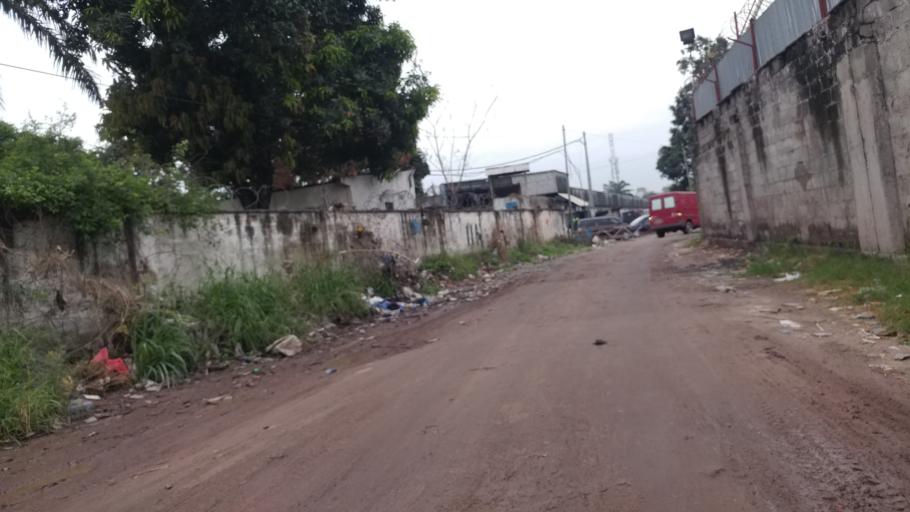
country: CD
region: Kinshasa
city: Kinshasa
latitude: -4.3219
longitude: 15.2757
